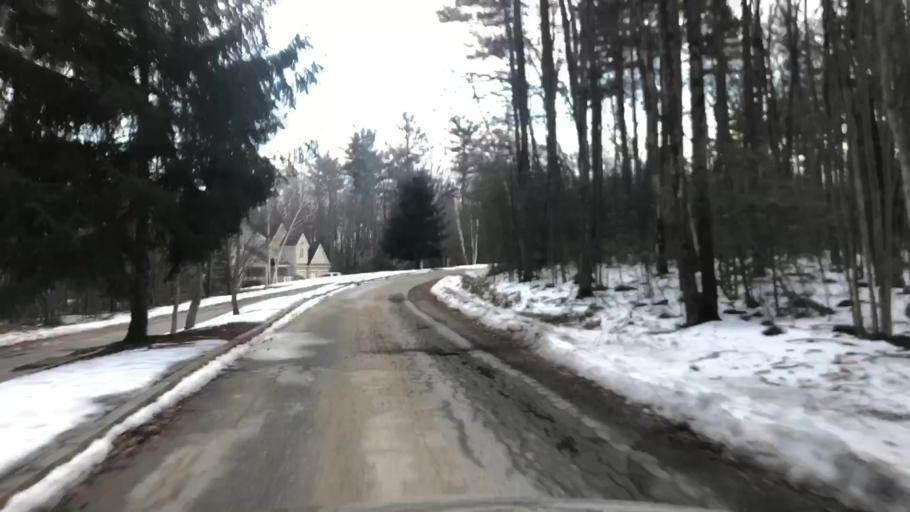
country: US
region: New Hampshire
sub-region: Hillsborough County
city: Milford
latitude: 42.8496
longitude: -71.6216
